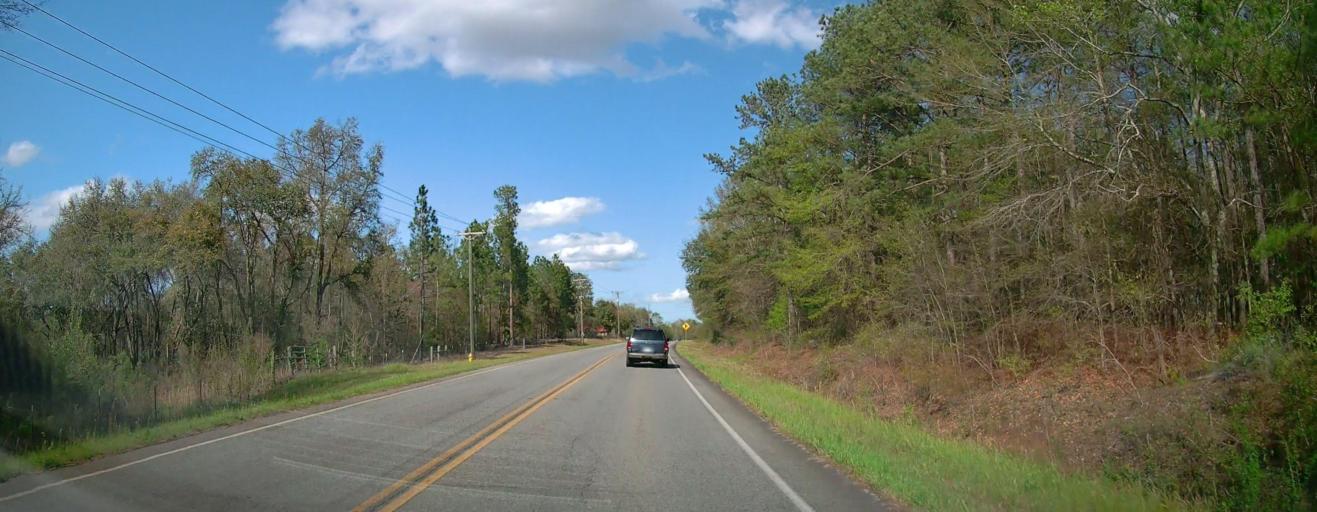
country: US
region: Georgia
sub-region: Baldwin County
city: Hardwick
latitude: 33.0031
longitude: -83.2544
